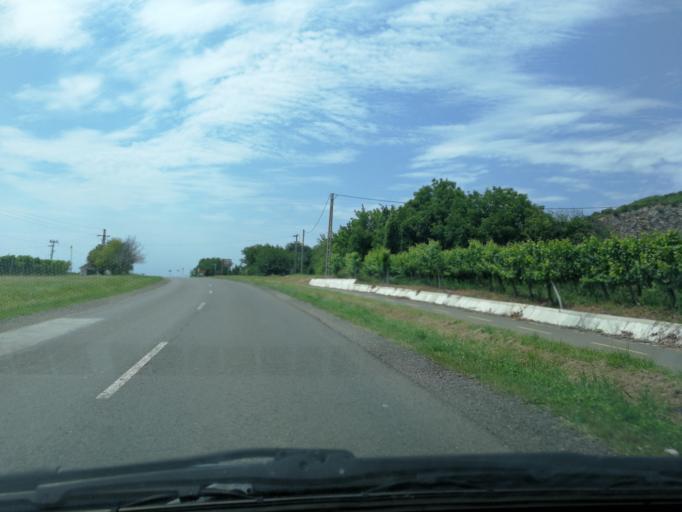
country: HU
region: Baranya
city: Villany
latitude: 45.8567
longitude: 18.4351
